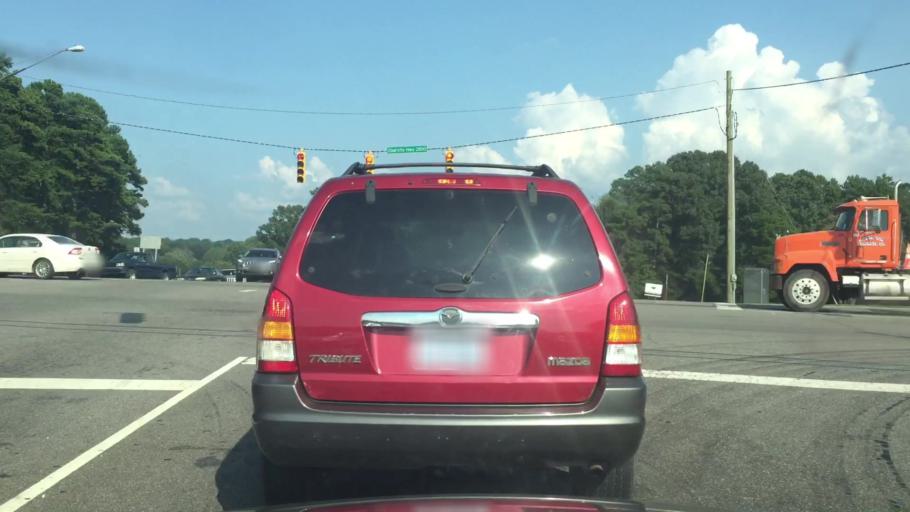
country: US
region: North Carolina
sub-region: Iredell County
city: Mooresville
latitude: 35.5789
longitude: -80.8425
